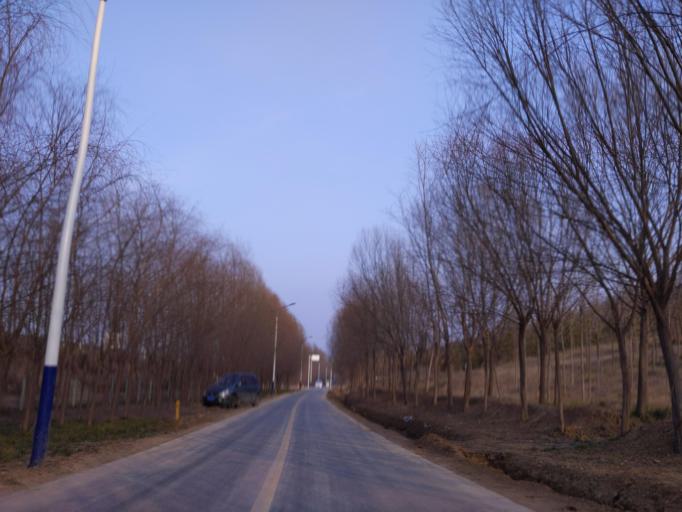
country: CN
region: Henan Sheng
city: Puyang
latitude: 35.8212
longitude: 115.0109
